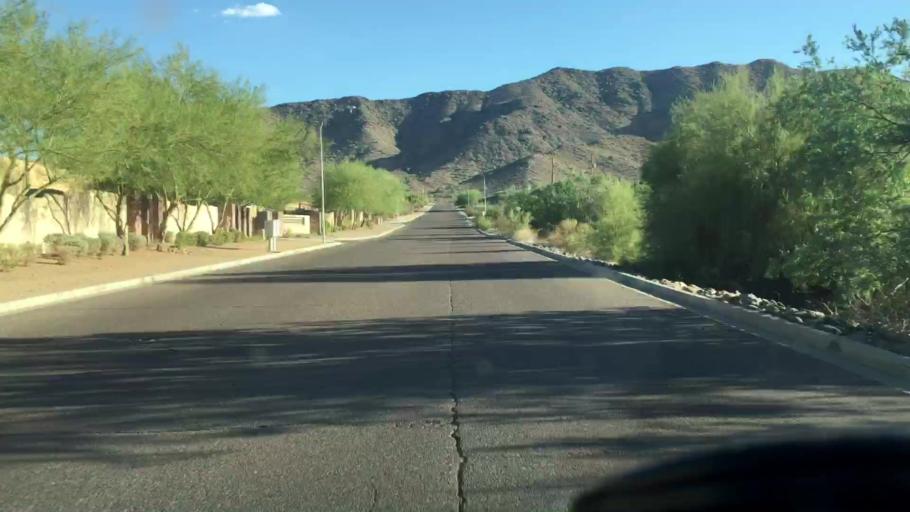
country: US
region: Arizona
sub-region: Maricopa County
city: Laveen
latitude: 33.3618
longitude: -112.0988
